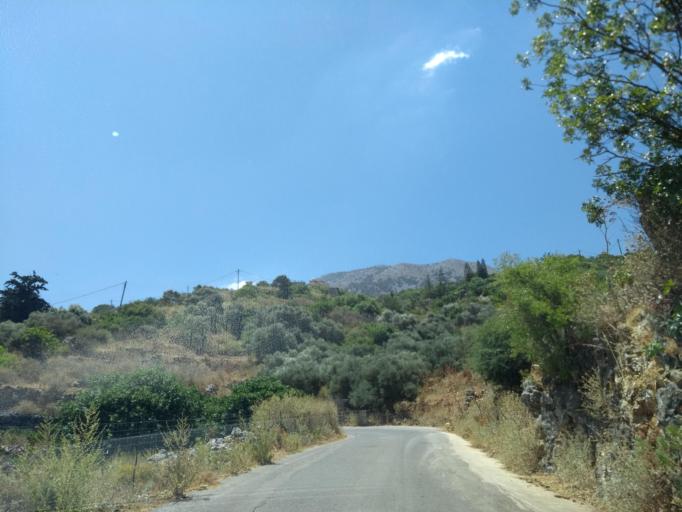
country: GR
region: Crete
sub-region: Nomos Chanias
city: Georgioupolis
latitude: 35.3171
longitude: 24.2907
